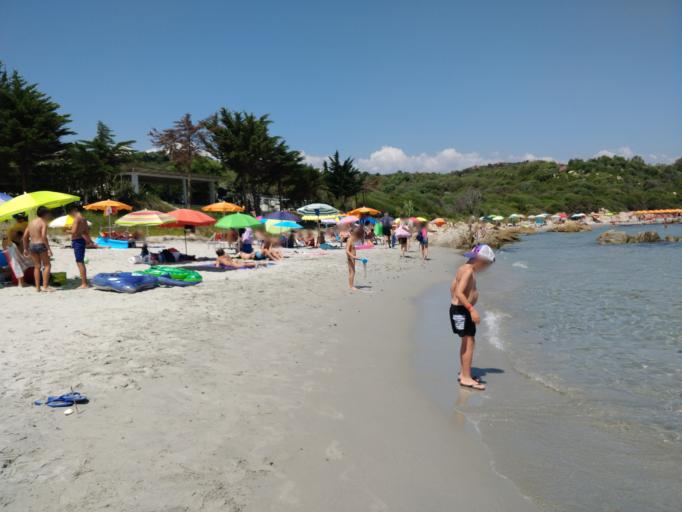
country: IT
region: Sardinia
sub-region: Provincia di Ogliastra
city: Tortoli
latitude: 39.8808
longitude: 9.6825
